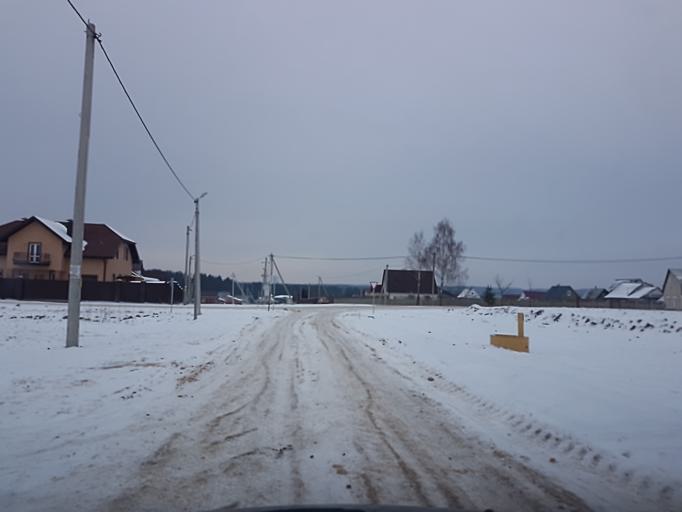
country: BY
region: Minsk
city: Rakaw
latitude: 53.9616
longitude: 27.0417
